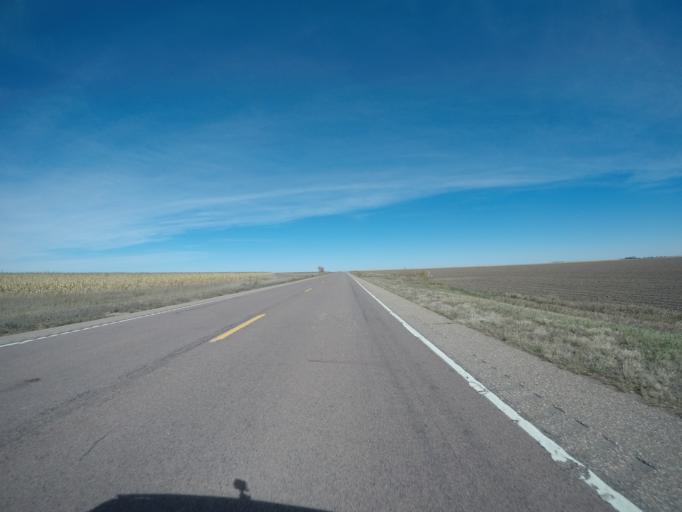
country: US
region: Colorado
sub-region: Kit Carson County
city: Burlington
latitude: 39.6658
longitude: -102.4267
